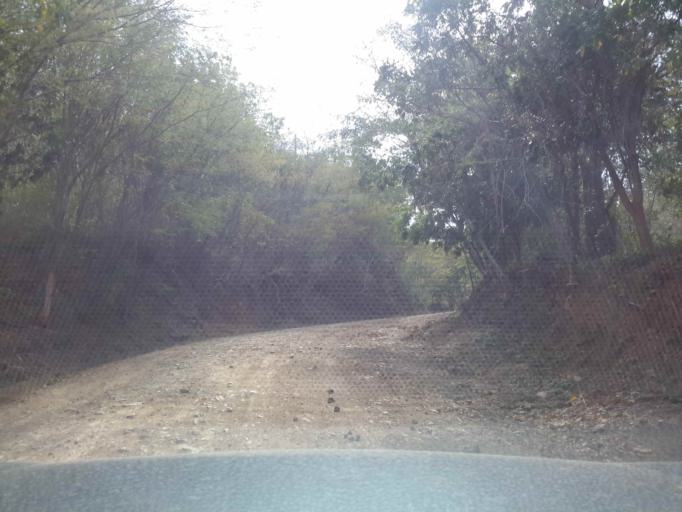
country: NI
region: Rivas
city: San Juan del Sur
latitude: 11.1837
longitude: -85.8118
